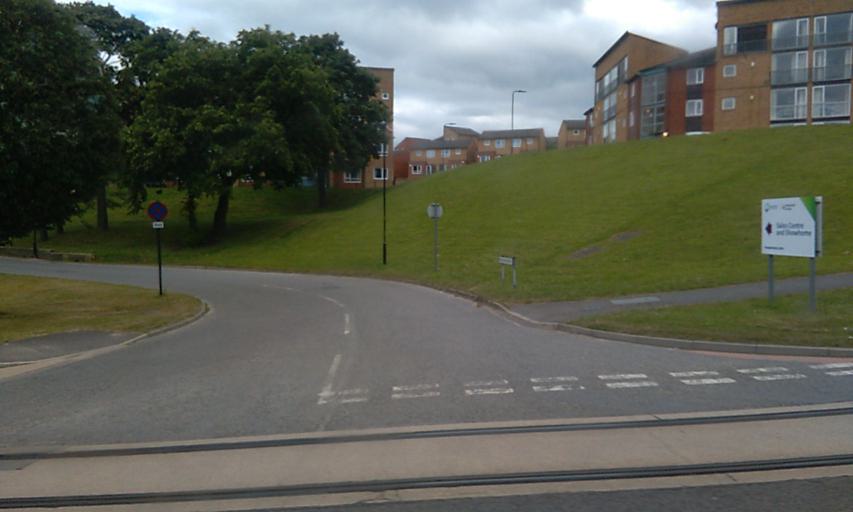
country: GB
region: England
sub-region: Sheffield
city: Sheffield
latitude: 53.3663
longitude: -1.4560
